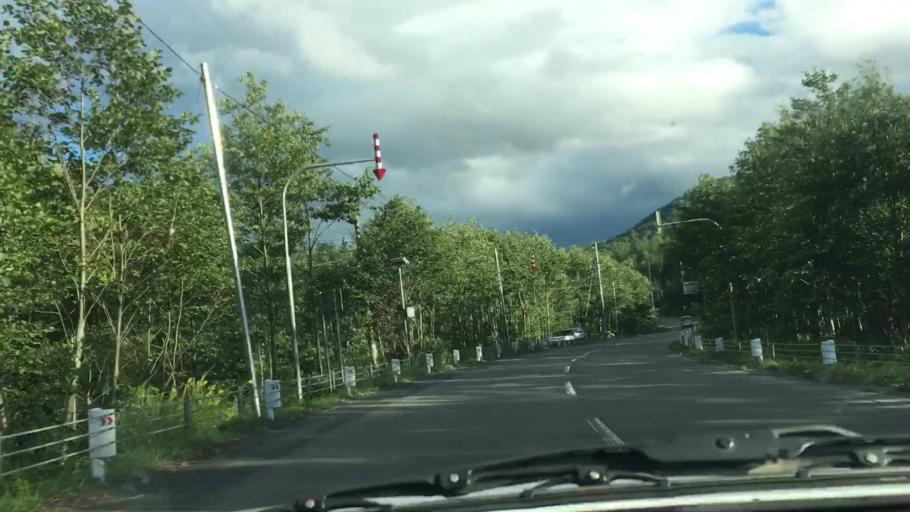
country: JP
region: Hokkaido
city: Shimo-furano
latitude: 43.1218
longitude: 142.6803
